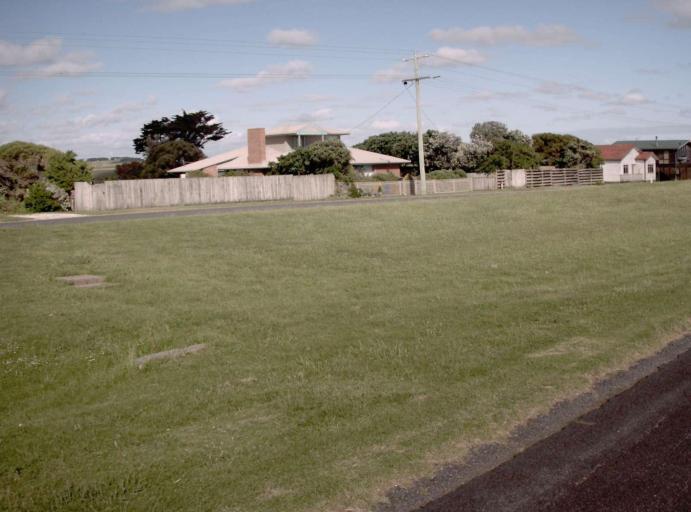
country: AU
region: Victoria
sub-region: Bass Coast
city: North Wonthaggi
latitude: -38.5512
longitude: 145.4784
